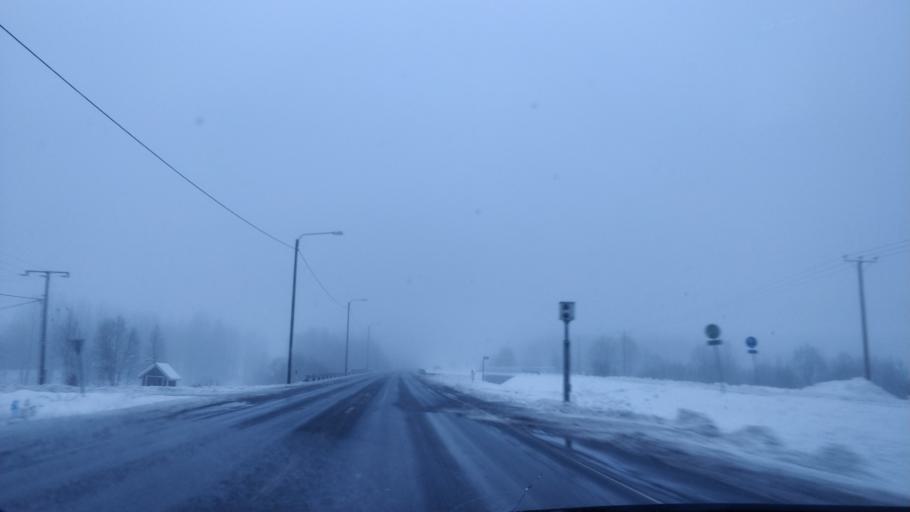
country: FI
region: Lapland
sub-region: Kemi-Tornio
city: Tervola
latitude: 66.1399
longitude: 24.9427
